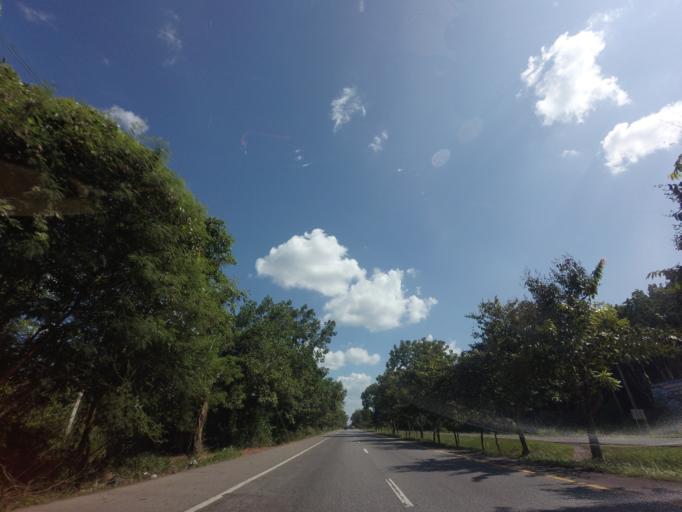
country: TH
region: Rayong
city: Wang Chan
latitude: 12.9583
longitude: 101.5057
